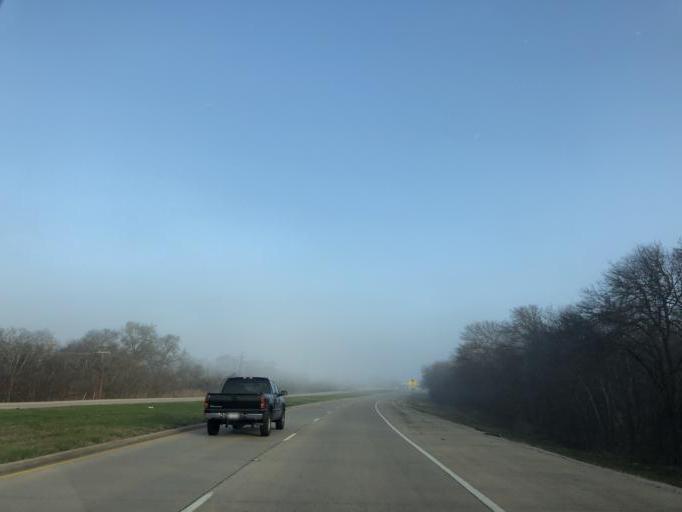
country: US
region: Texas
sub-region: Dallas County
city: Duncanville
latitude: 32.6672
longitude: -96.9849
